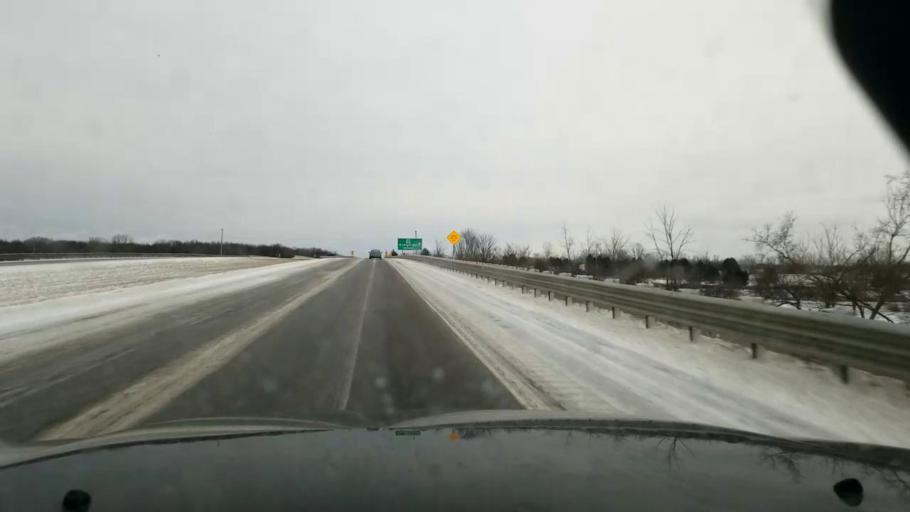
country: US
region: Michigan
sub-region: Jackson County
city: Jackson
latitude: 42.2573
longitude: -84.4766
